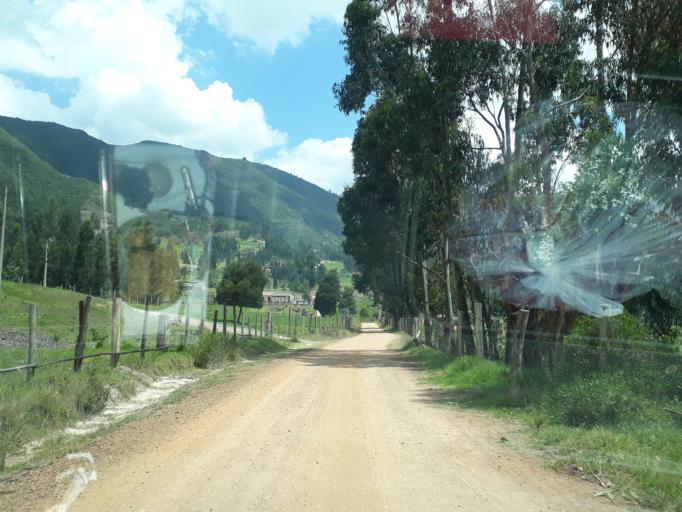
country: CO
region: Boyaca
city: Floresta
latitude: 5.8492
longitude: -72.9525
